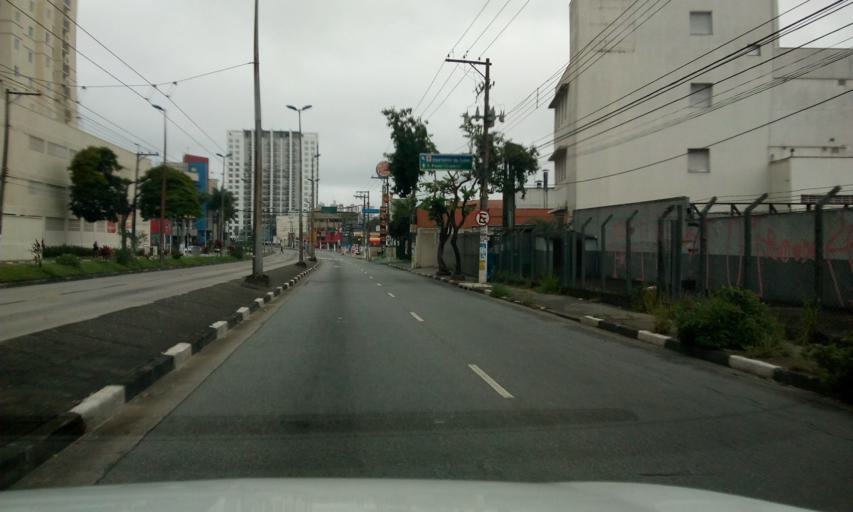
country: BR
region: Sao Paulo
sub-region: Diadema
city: Diadema
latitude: -23.6857
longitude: -46.6150
